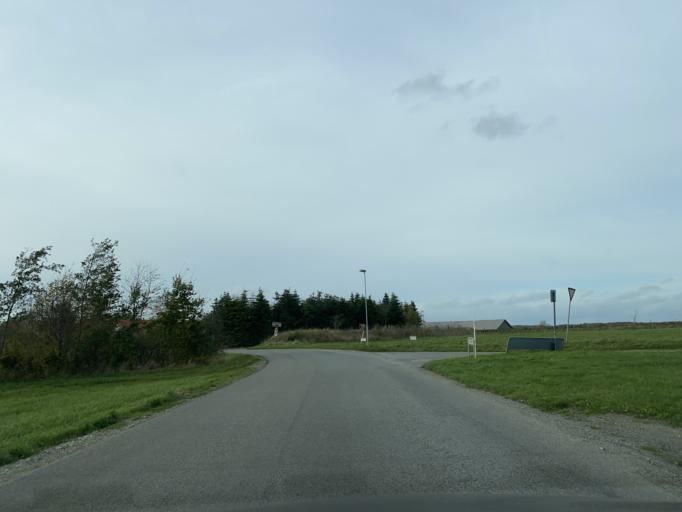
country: DK
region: Central Jutland
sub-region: Arhus Kommune
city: Framlev
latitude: 56.1645
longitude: 9.9962
